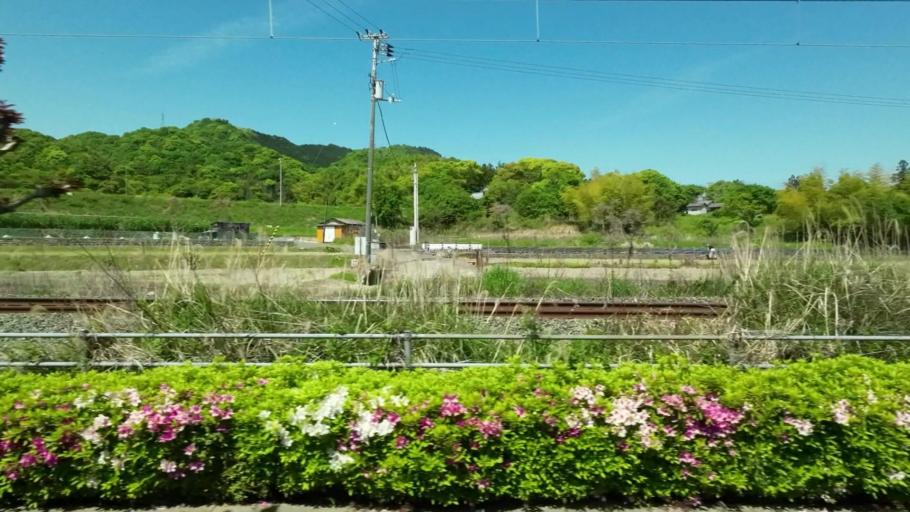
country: JP
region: Ehime
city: Hojo
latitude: 34.0849
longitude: 132.9845
